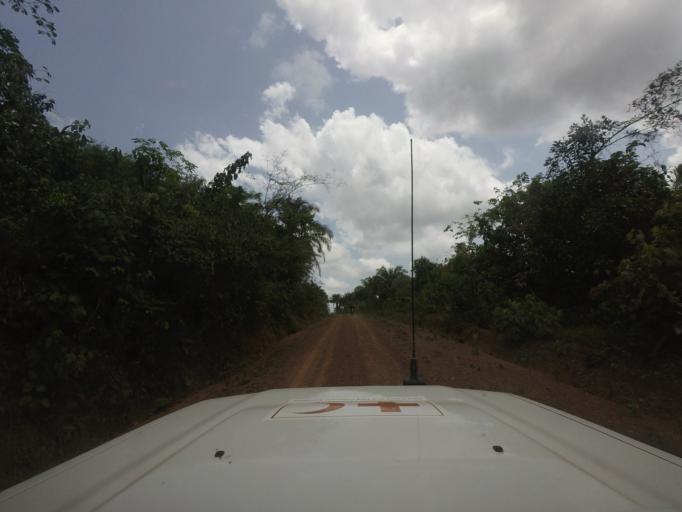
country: GN
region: Nzerekore
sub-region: Yomou
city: Yomou
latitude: 7.2682
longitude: -9.1857
